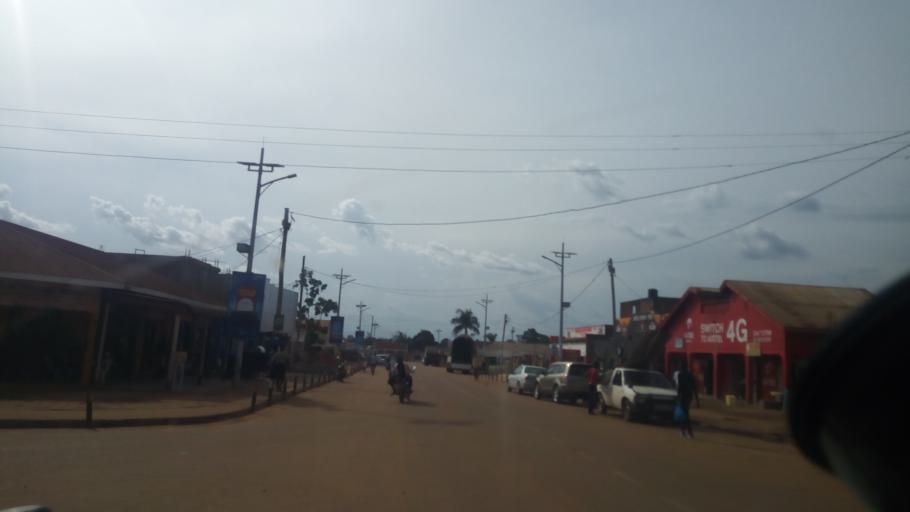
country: UG
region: Northern Region
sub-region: Lira District
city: Lira
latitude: 2.2381
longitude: 32.8913
